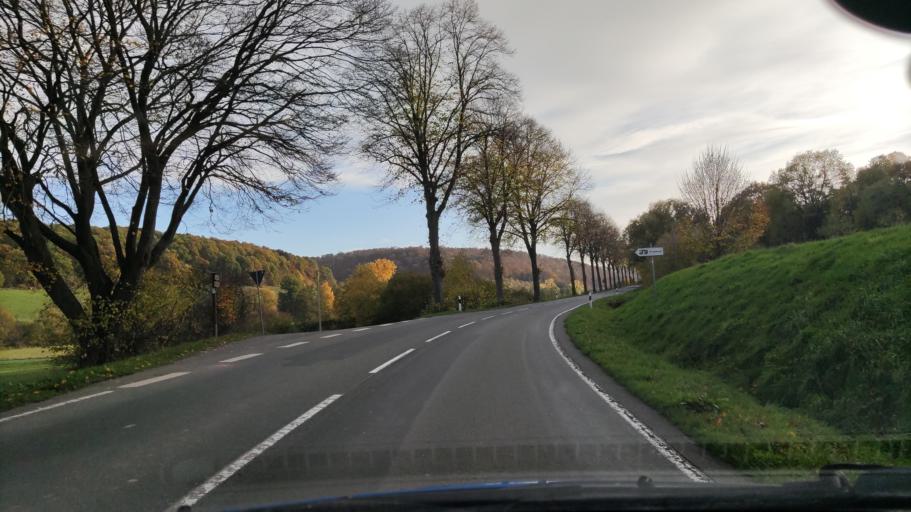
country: DE
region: Lower Saxony
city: Dassel
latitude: 51.7583
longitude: 9.7613
